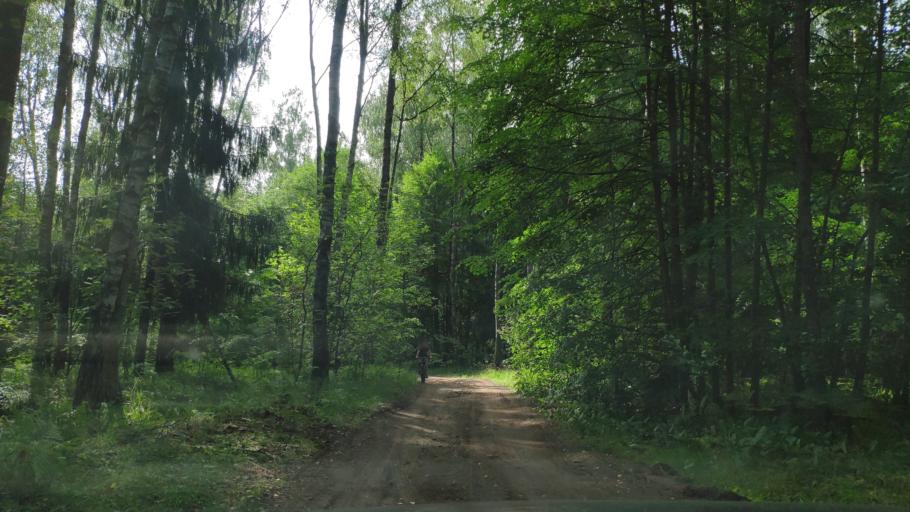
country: BY
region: Minsk
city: Zaslawye
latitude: 53.9686
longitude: 27.2948
